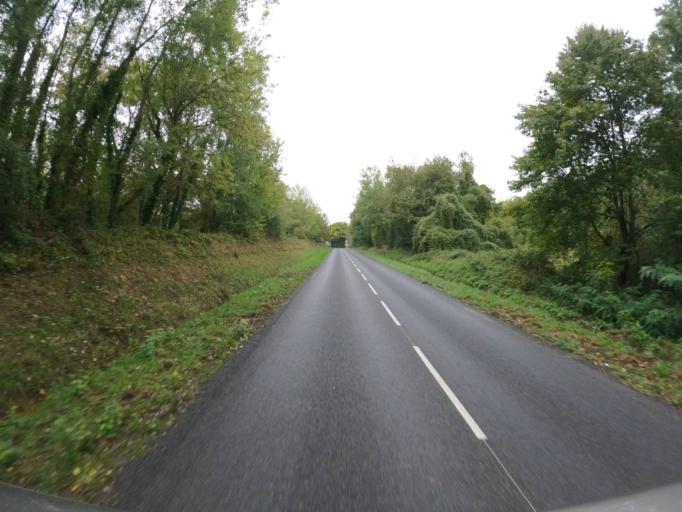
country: FR
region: Ile-de-France
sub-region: Departement de Seine-et-Marne
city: Serris
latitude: 48.8250
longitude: 2.7680
